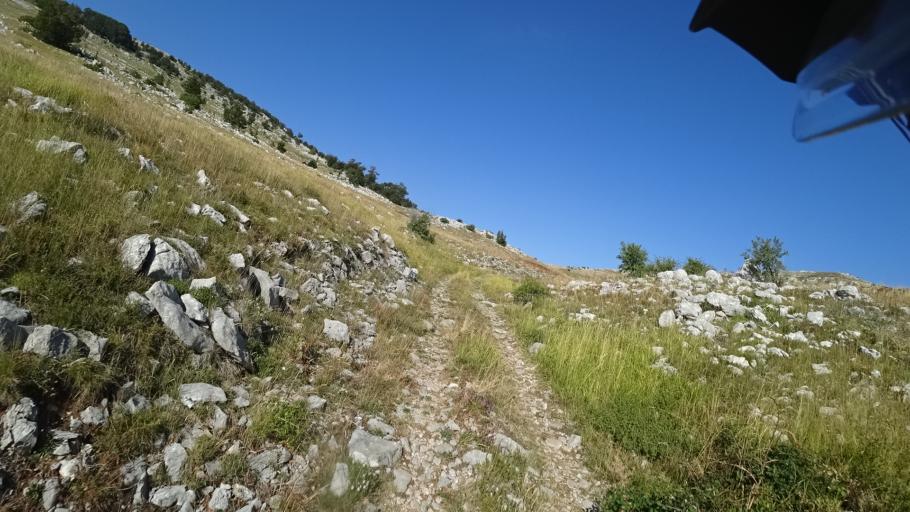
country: HR
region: Sibensko-Kniniska
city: Knin
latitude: 44.2017
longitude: 16.1552
